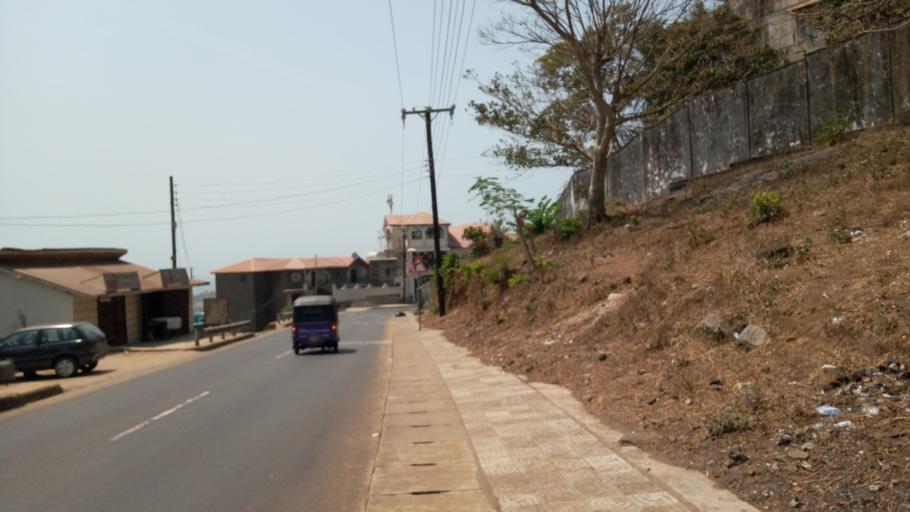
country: SL
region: Western Area
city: Freetown
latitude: 8.4824
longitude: -13.2665
